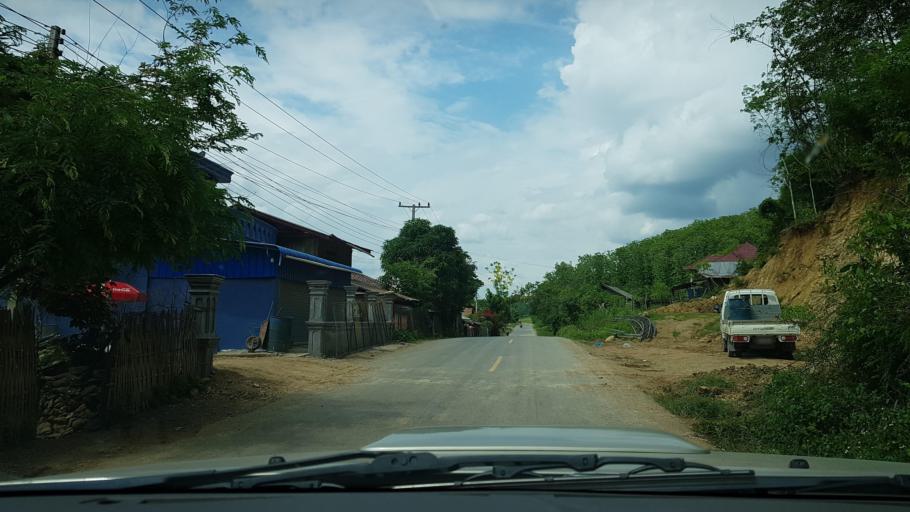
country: LA
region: Loungnamtha
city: Muang Nale
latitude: 20.2552
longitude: 101.5879
